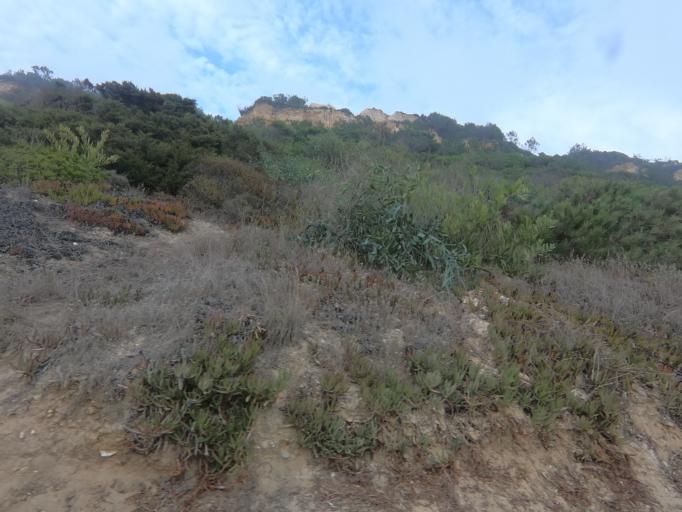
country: PT
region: Setubal
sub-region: Almada
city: Charneca
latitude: 38.5602
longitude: -9.1902
